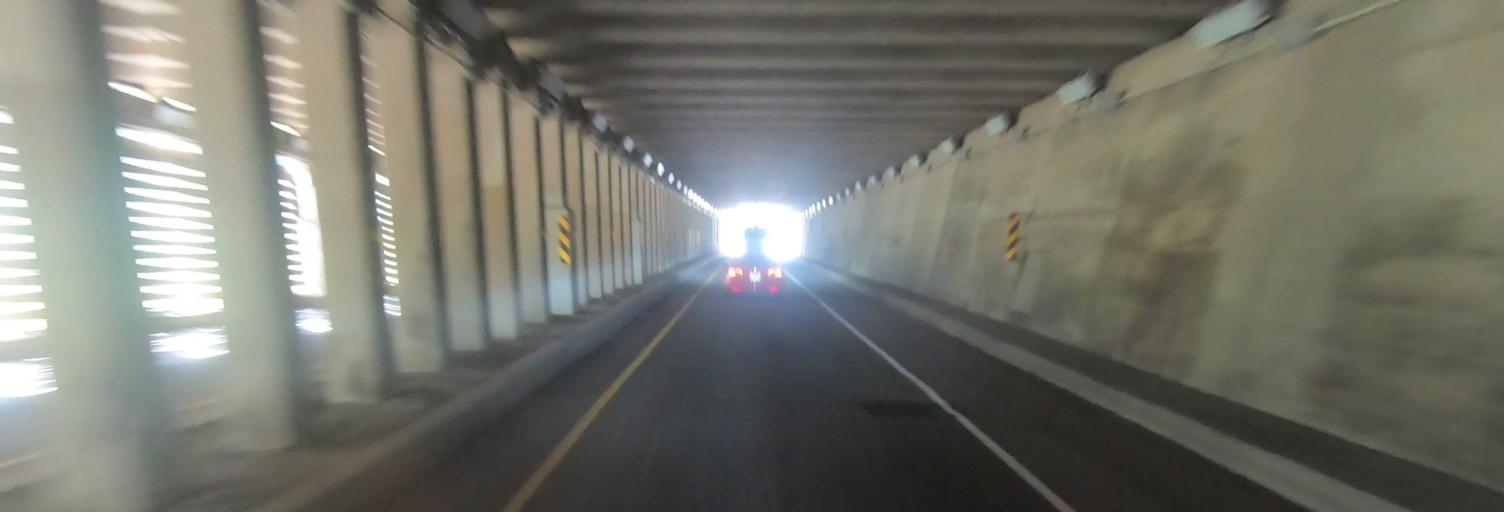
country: CA
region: British Columbia
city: Golden
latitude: 51.3237
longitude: -117.4807
